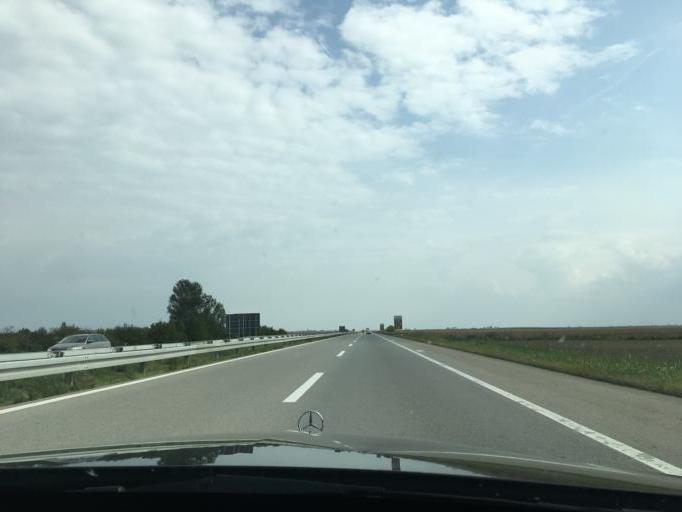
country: RS
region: Autonomna Pokrajina Vojvodina
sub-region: Sremski Okrug
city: Sremska Mitrovica
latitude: 44.9985
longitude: 19.6632
